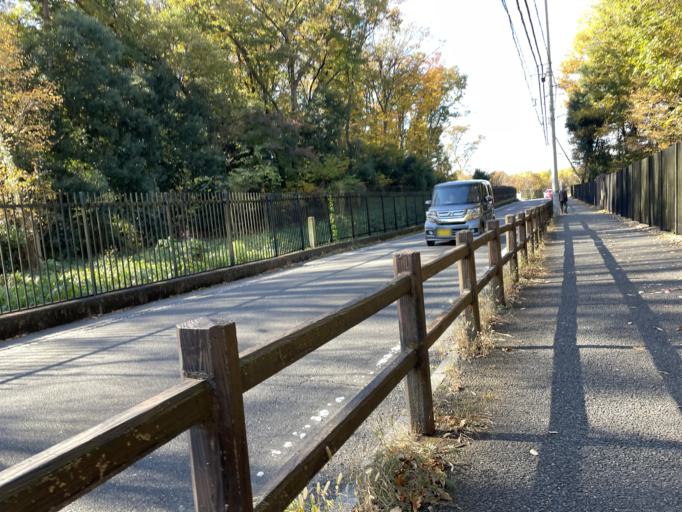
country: JP
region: Saitama
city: Asaka
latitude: 35.7954
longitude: 139.5619
